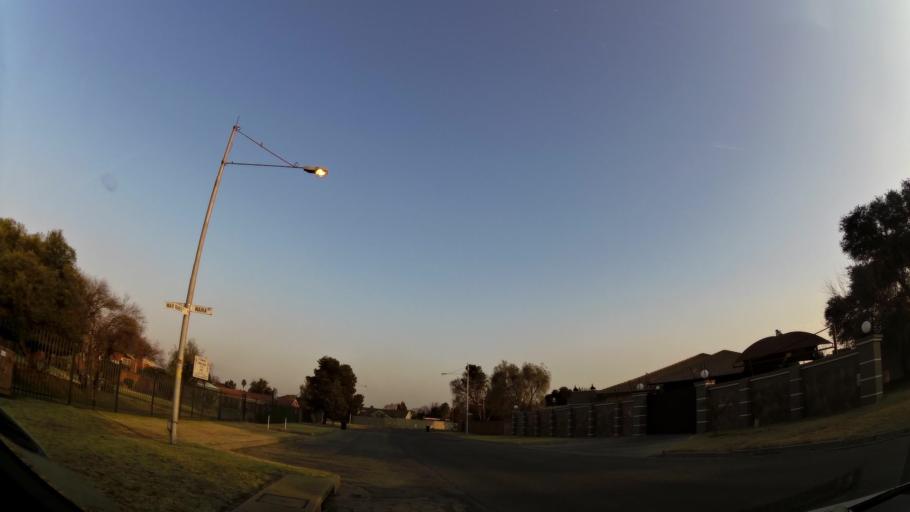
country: ZA
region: Gauteng
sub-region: Ekurhuleni Metropolitan Municipality
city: Springs
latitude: -26.3099
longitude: 28.4515
